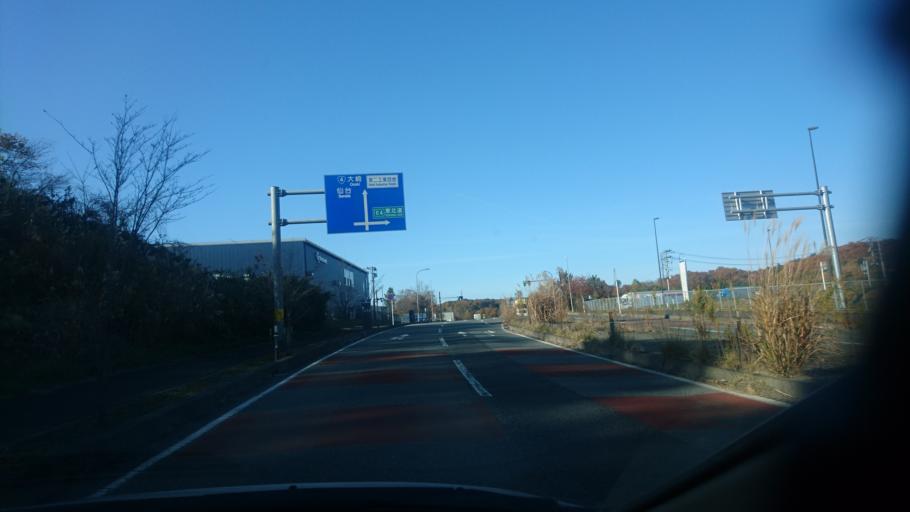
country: JP
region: Miyagi
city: Tomiya
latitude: 38.4680
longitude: 140.9082
